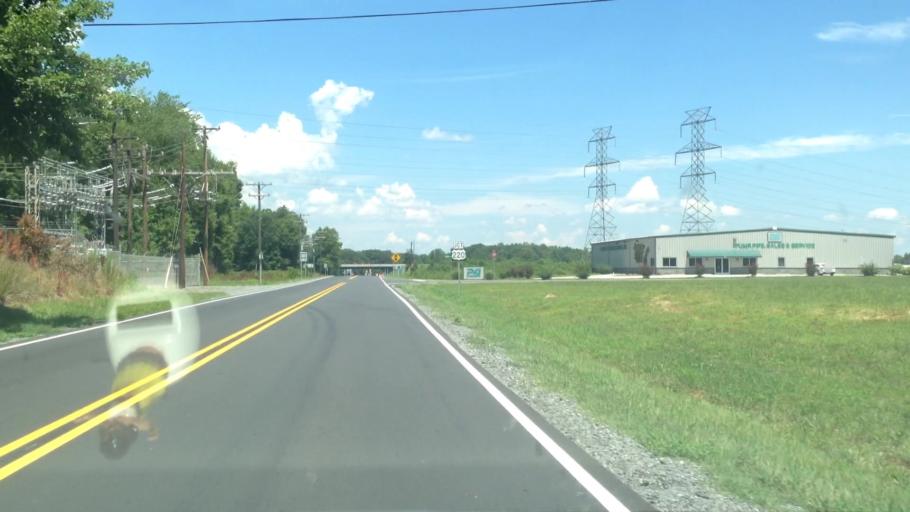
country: US
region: North Carolina
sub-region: Guilford County
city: Summerfield
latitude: 36.2434
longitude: -79.9259
